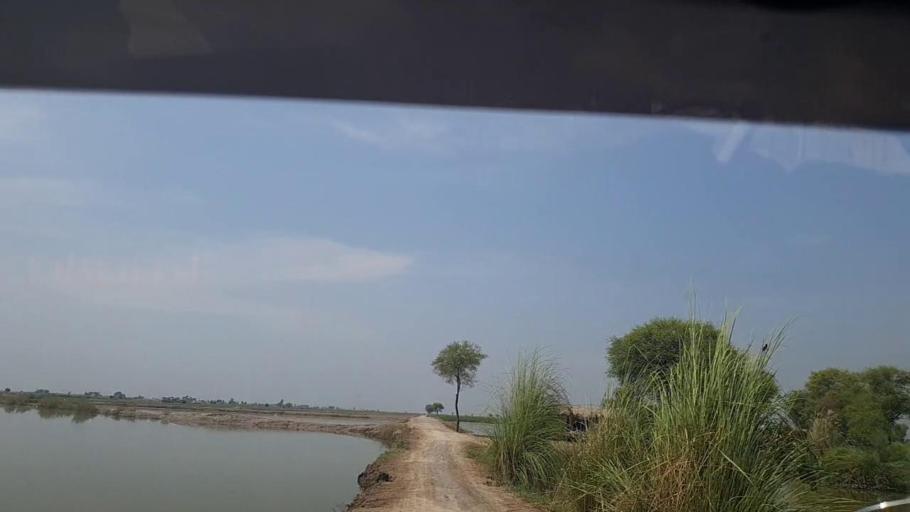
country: PK
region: Sindh
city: Thul
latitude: 28.2094
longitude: 68.6891
